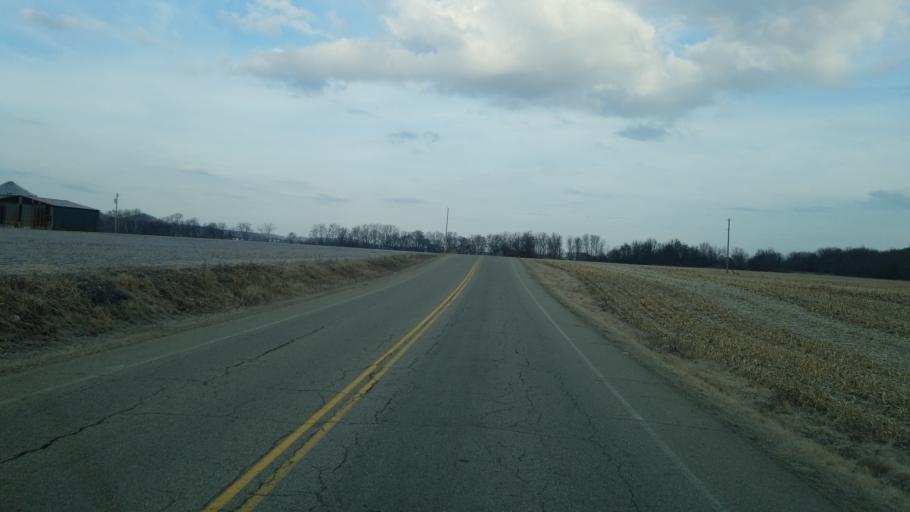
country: US
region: Ohio
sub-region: Pike County
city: Waverly
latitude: 39.2253
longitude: -82.8526
